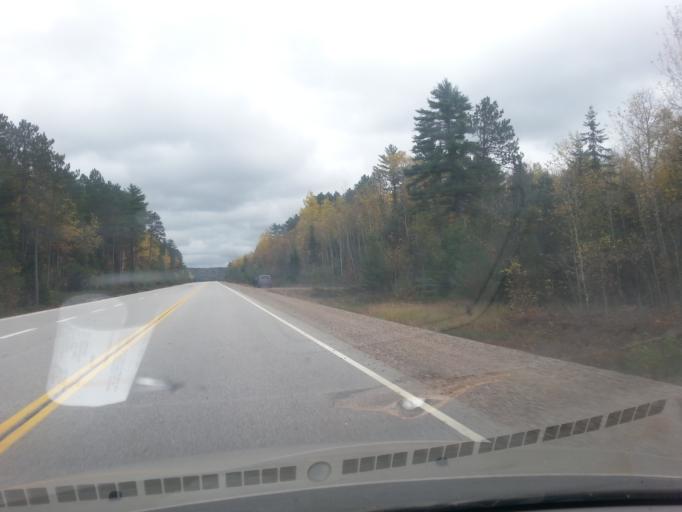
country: CA
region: Ontario
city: Mattawa
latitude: 46.2826
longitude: -78.4105
